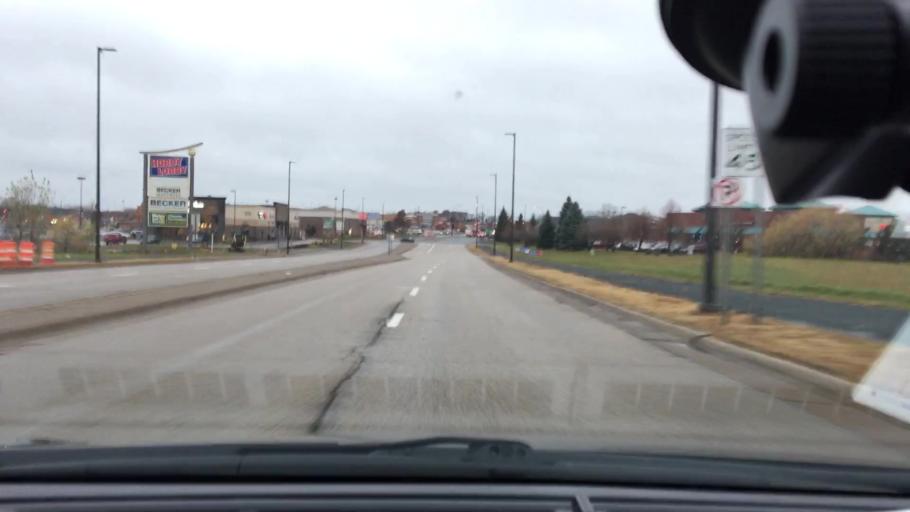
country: US
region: Minnesota
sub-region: Hennepin County
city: Maple Grove
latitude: 45.1252
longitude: -93.4862
